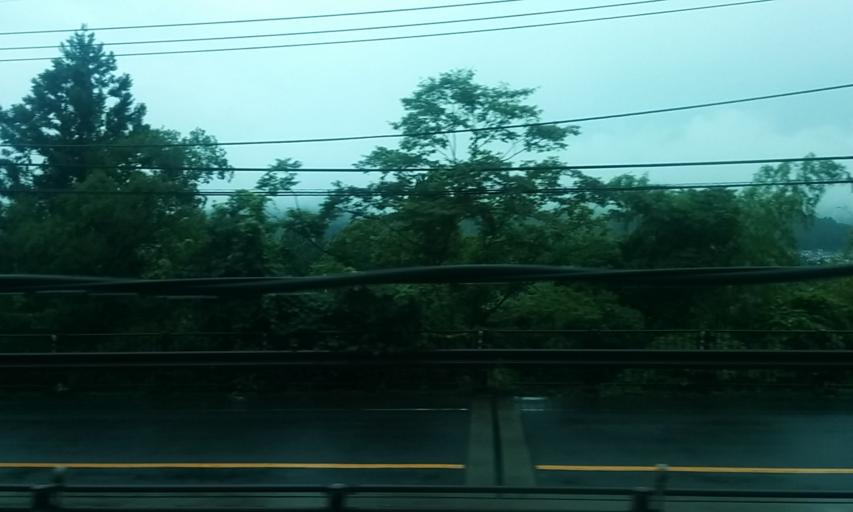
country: JP
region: Tokyo
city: Ome
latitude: 35.7941
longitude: 139.2269
